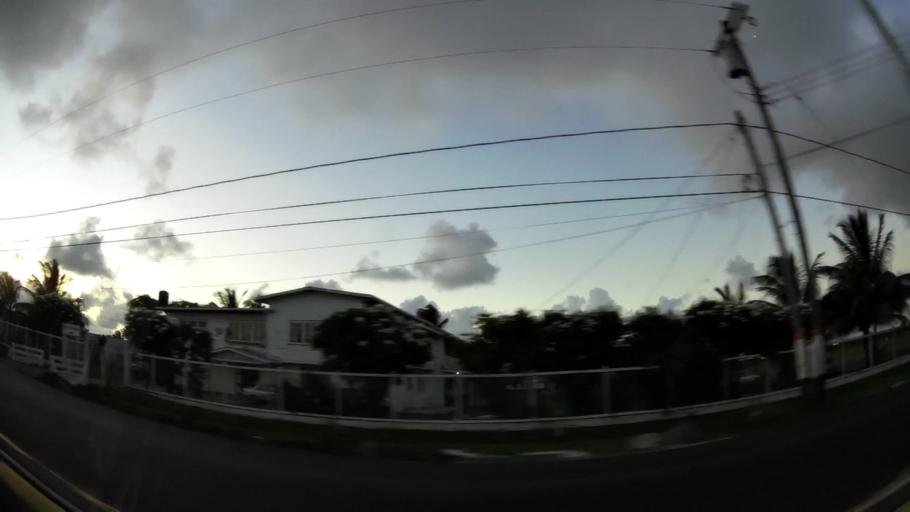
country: GY
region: Demerara-Mahaica
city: Georgetown
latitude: 6.8229
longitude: -58.1548
